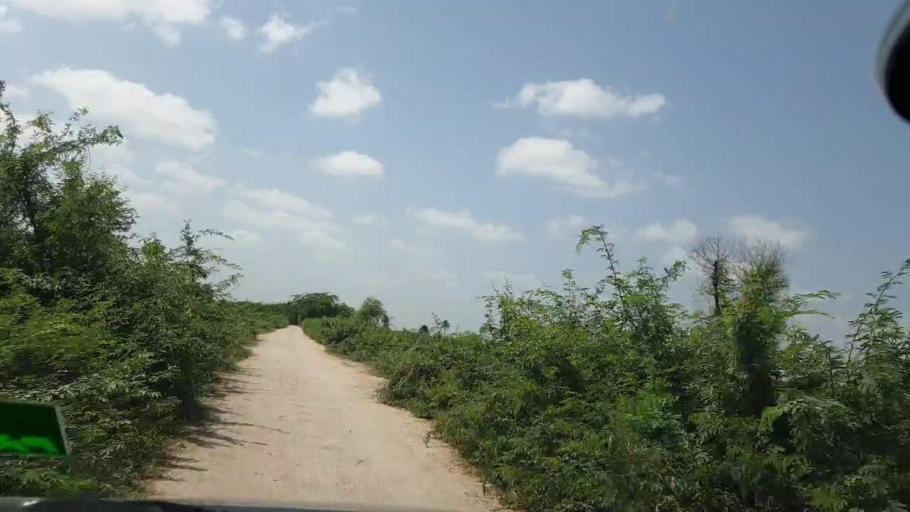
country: PK
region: Sindh
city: Kadhan
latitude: 24.5517
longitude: 69.2103
